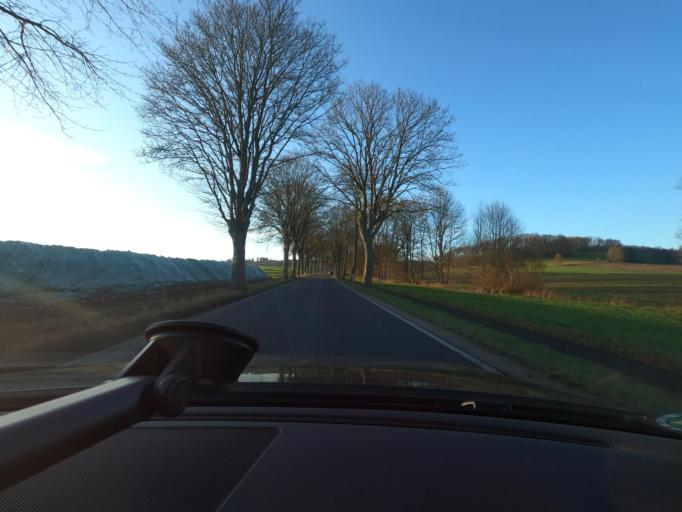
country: DE
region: Lower Saxony
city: Eisdorf am Harz
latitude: 51.7722
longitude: 10.1813
